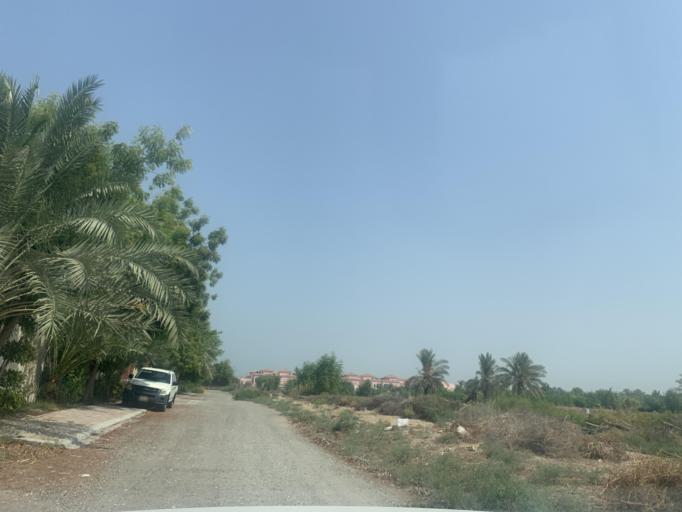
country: BH
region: Central Governorate
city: Madinat Hamad
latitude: 26.1655
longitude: 50.4592
